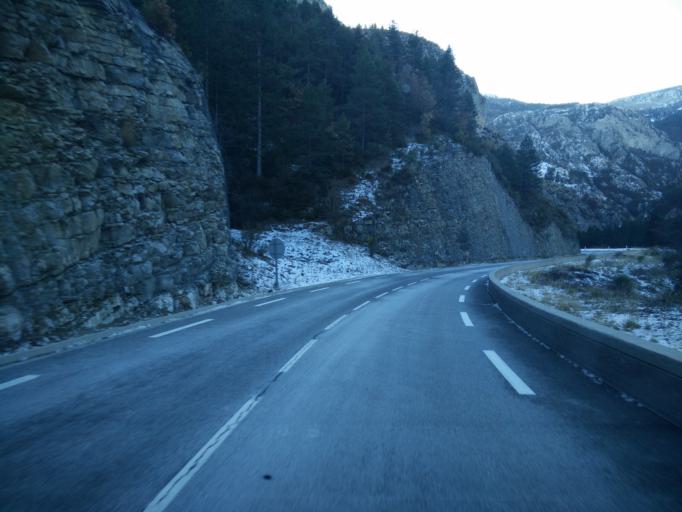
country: FR
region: Provence-Alpes-Cote d'Azur
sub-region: Departement des Alpes-de-Haute-Provence
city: Annot
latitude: 43.9468
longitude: 6.6896
